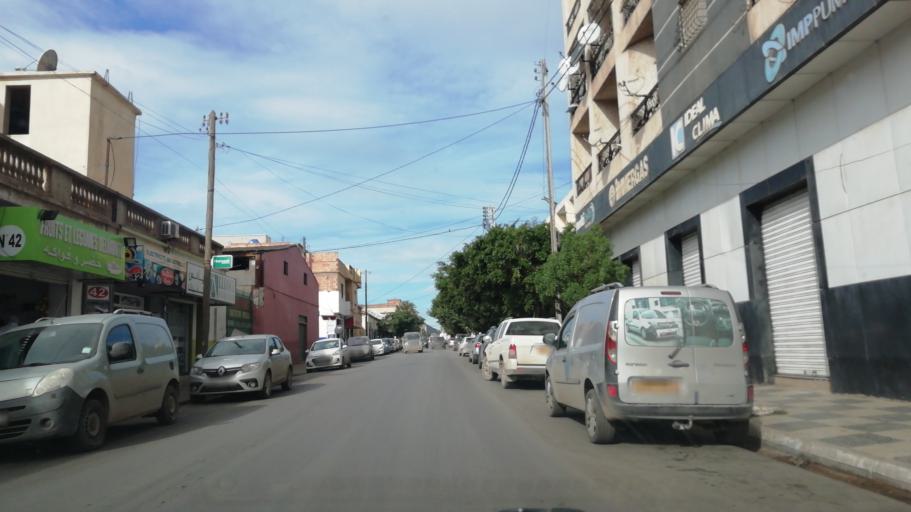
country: DZ
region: Oran
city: Oran
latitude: 35.6905
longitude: -0.6261
